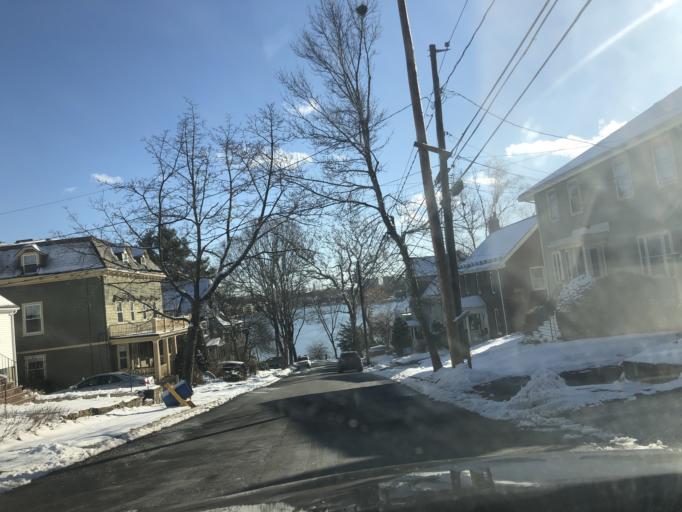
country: US
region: Massachusetts
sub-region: Middlesex County
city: Arlington
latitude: 42.4120
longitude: -71.1552
